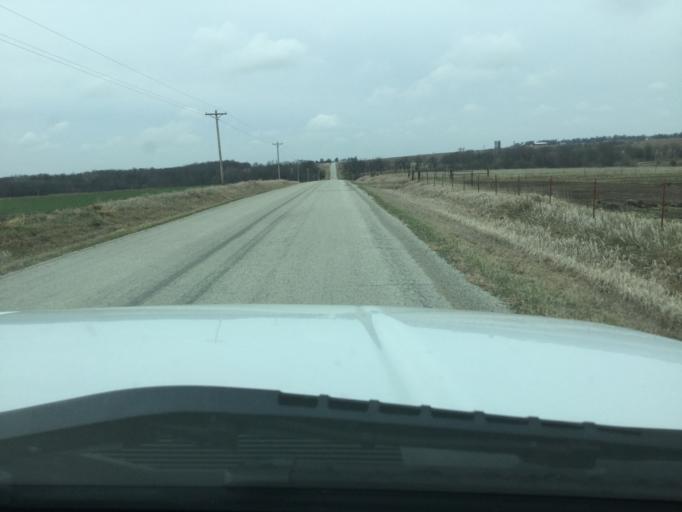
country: US
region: Kansas
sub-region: Nemaha County
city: Sabetha
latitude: 39.8600
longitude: -95.7142
